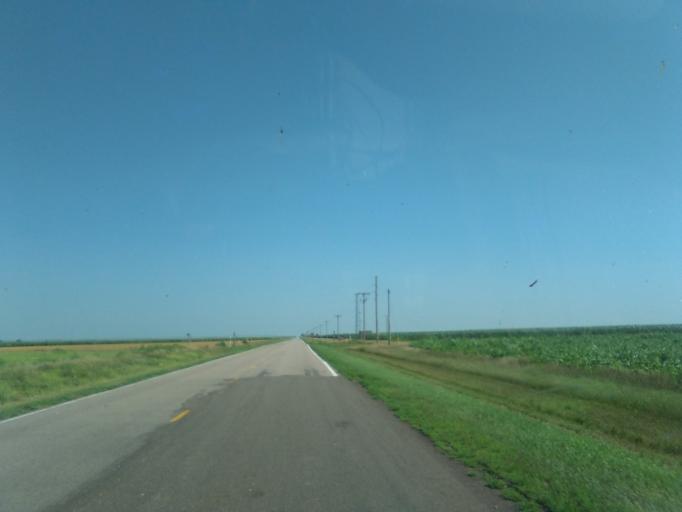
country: US
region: Kansas
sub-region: Cheyenne County
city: Saint Francis
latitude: 39.7703
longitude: -101.5420
